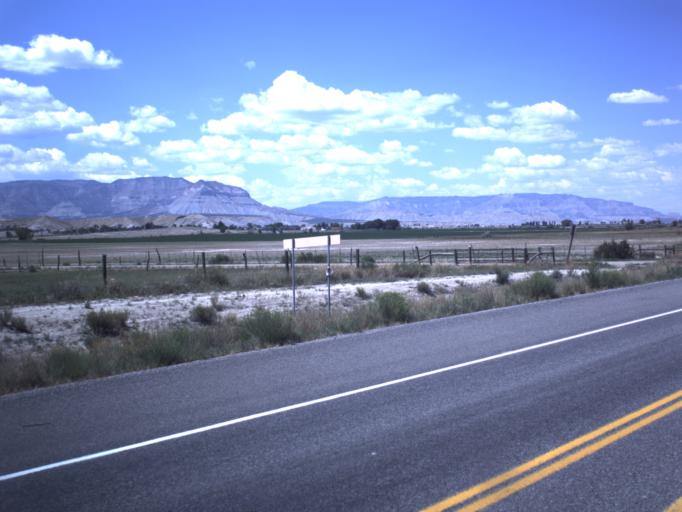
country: US
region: Utah
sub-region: Emery County
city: Castle Dale
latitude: 39.2236
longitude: -110.9965
